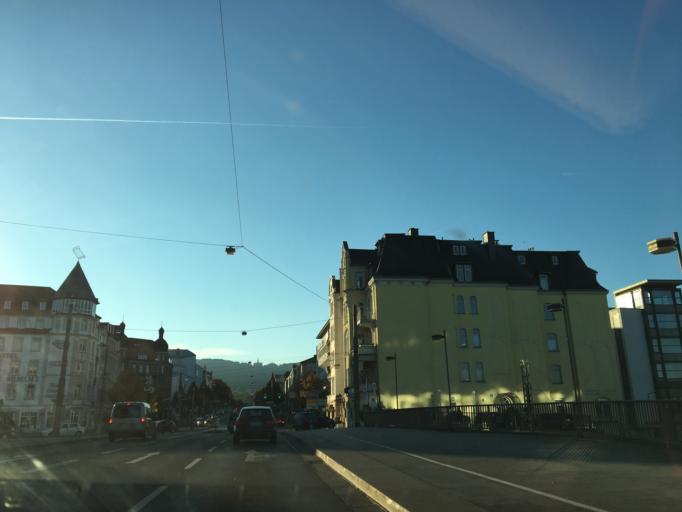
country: DE
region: Hesse
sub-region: Regierungsbezirk Kassel
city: Kassel
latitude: 51.3136
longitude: 9.4468
